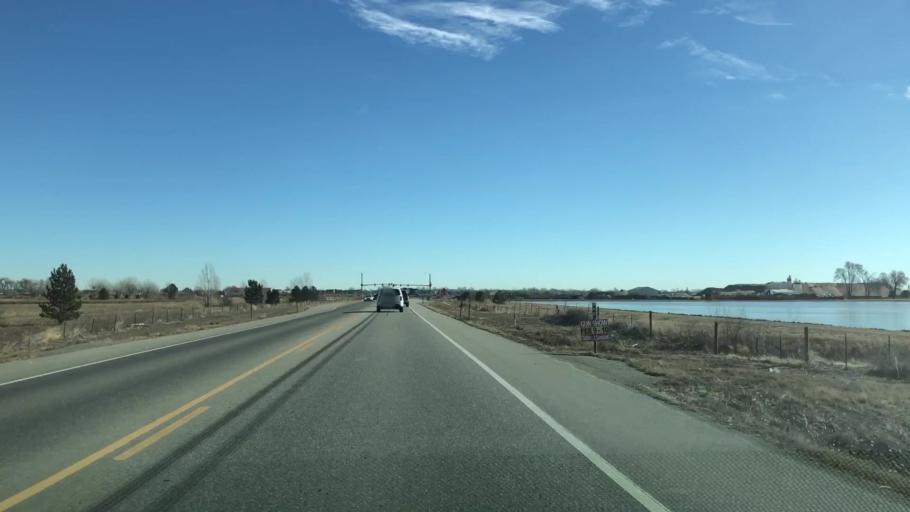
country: US
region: Colorado
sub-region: Weld County
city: Windsor
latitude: 40.4792
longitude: -104.9488
